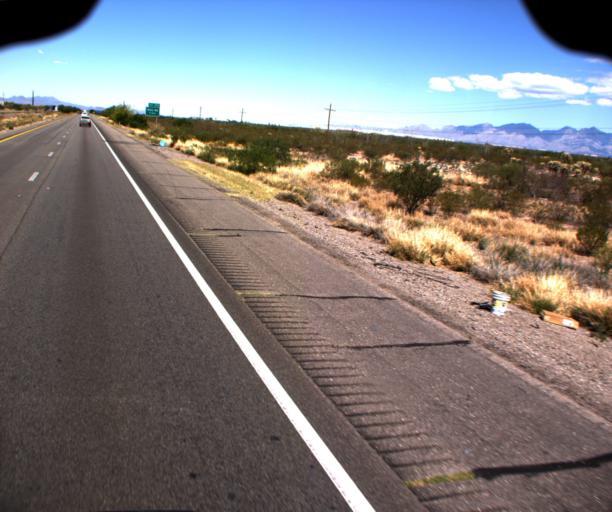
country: US
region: Arizona
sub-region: Pima County
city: Vail
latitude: 32.0709
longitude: -110.7883
